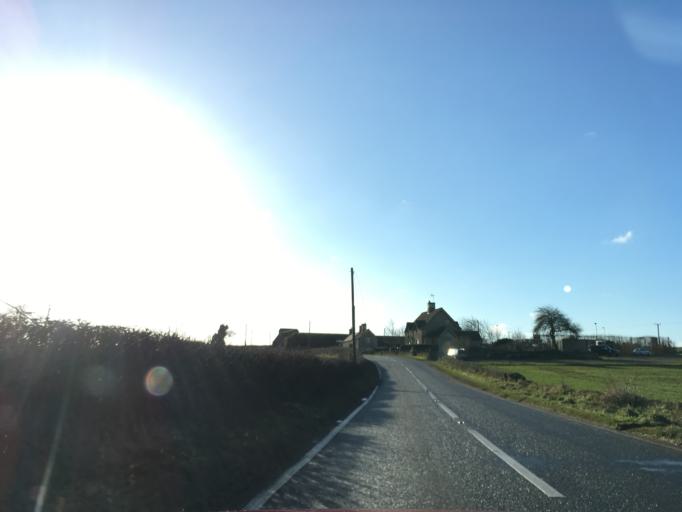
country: GB
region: England
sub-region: South Gloucestershire
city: Horton
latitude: 51.5285
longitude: -2.3091
